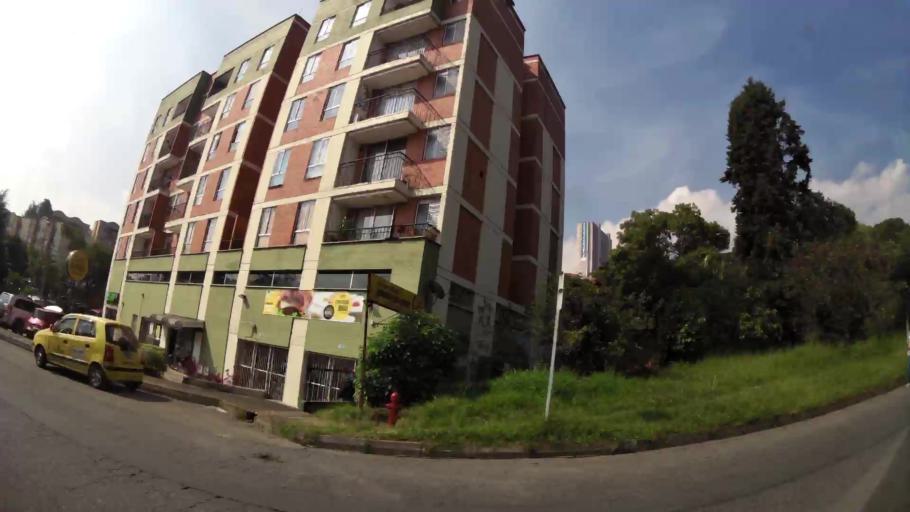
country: CO
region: Antioquia
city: La Estrella
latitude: 6.1704
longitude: -75.6307
